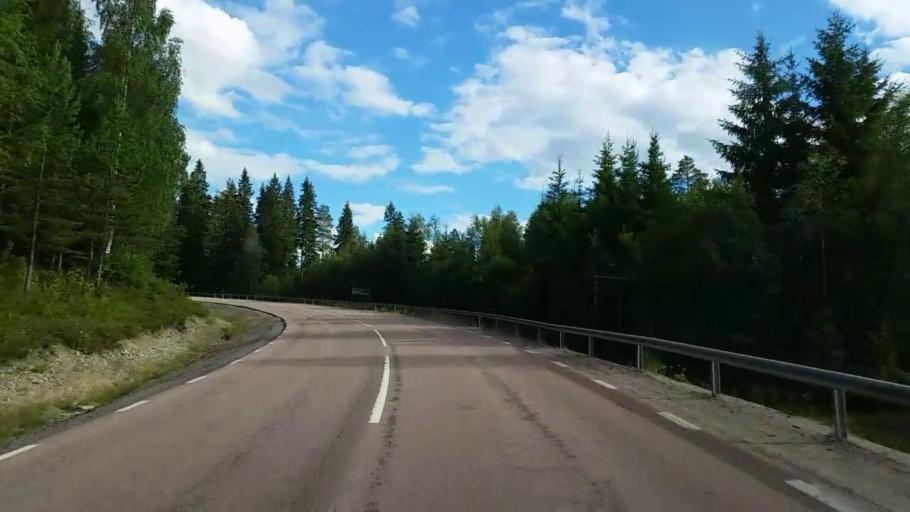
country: SE
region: Gaevleborg
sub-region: Ljusdals Kommun
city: Farila
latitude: 61.8922
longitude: 15.9084
